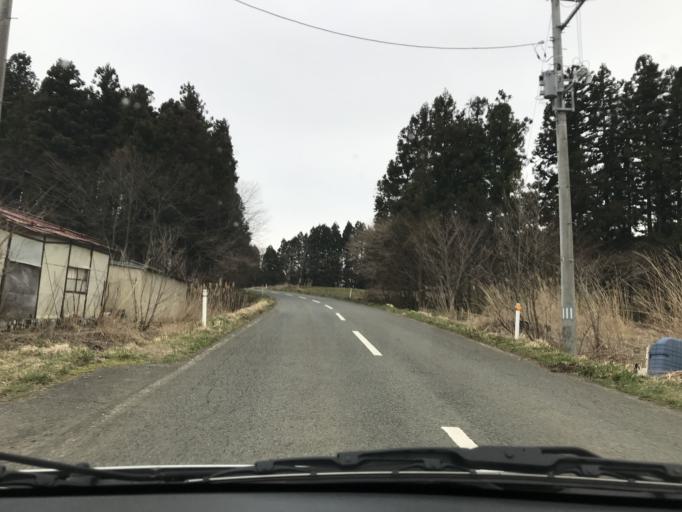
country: JP
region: Iwate
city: Mizusawa
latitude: 39.0932
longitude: 141.0687
